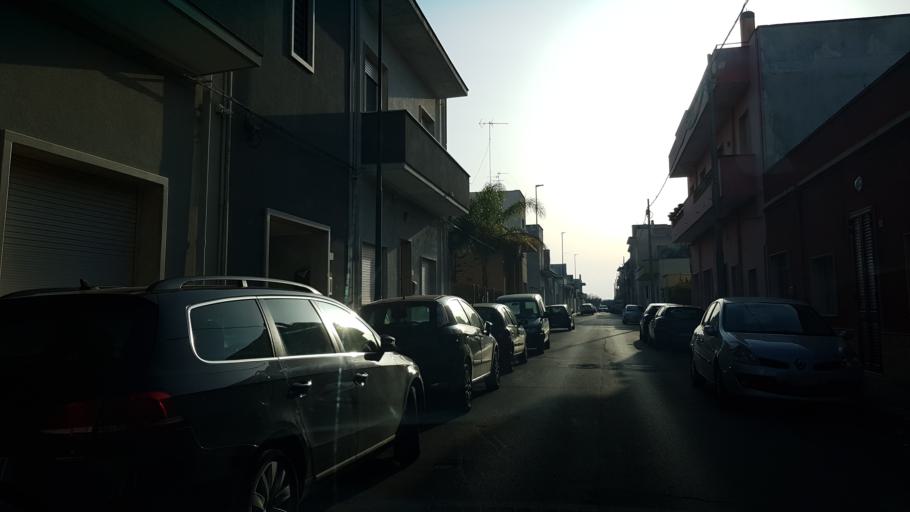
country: IT
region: Apulia
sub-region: Provincia di Lecce
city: Trepuzzi
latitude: 40.4071
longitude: 18.0653
